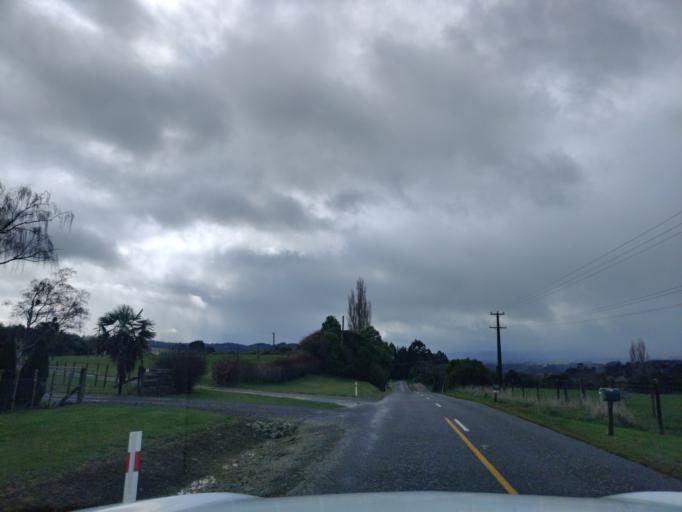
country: NZ
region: Manawatu-Wanganui
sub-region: Palmerston North City
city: Palmerston North
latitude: -40.1846
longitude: 175.7859
